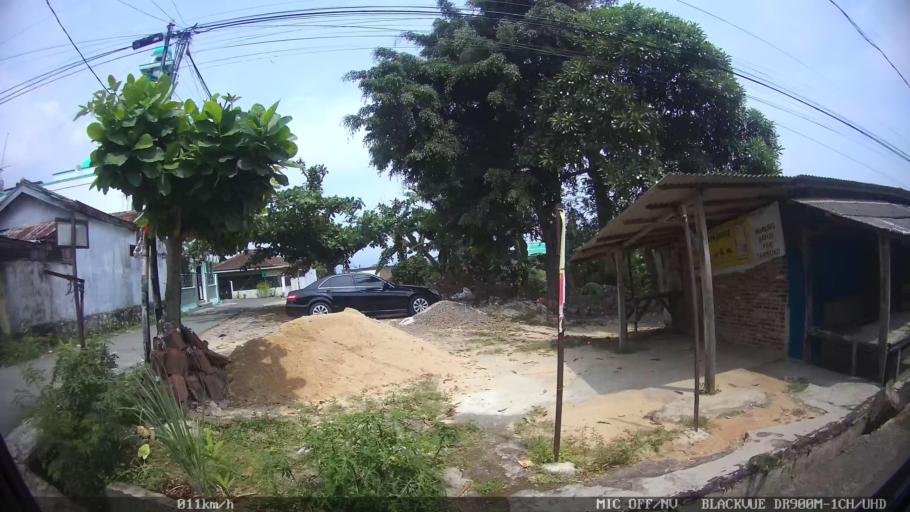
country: ID
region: Lampung
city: Bandarlampung
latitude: -5.4362
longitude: 105.2673
